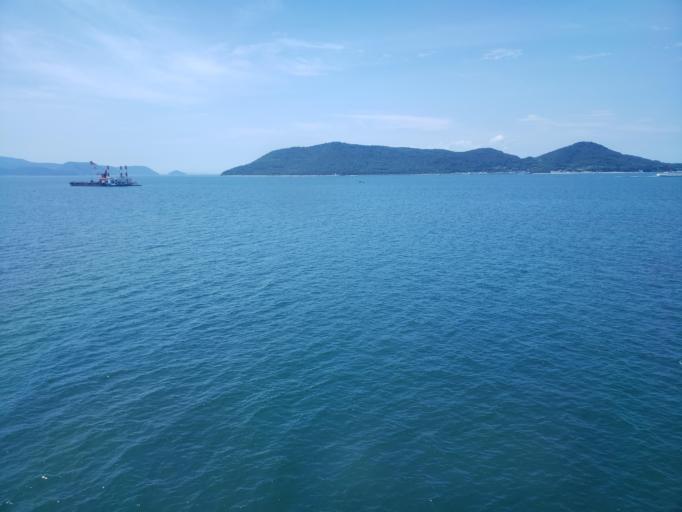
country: JP
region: Kagawa
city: Takamatsu-shi
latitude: 34.3713
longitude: 134.0761
